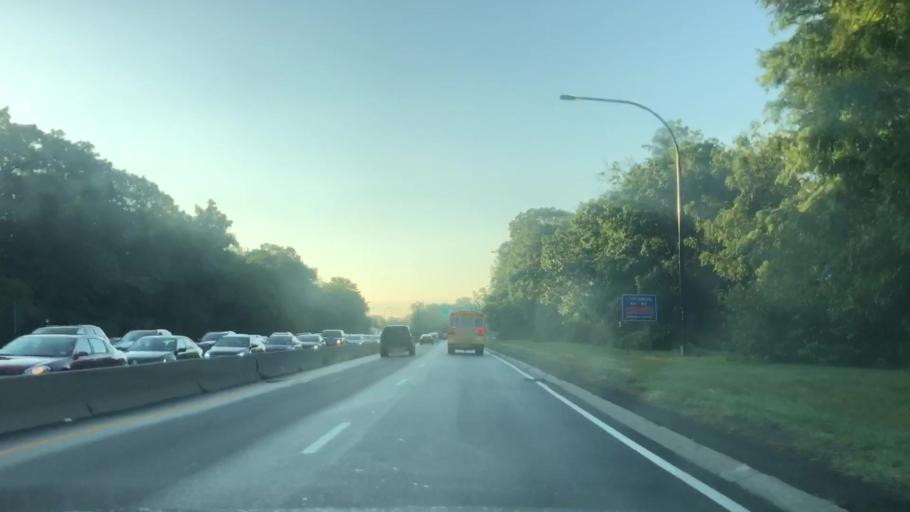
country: US
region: New York
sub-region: Nassau County
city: North Bellmore
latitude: 40.7036
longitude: -73.5230
